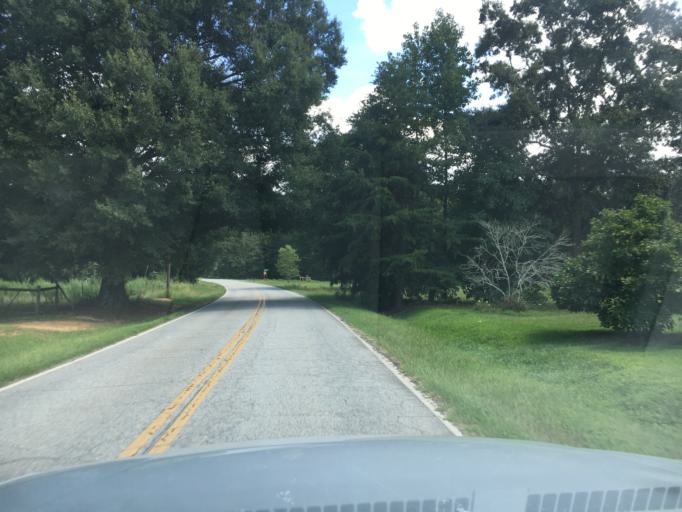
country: US
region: South Carolina
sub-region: Anderson County
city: Belton
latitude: 34.5671
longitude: -82.4838
